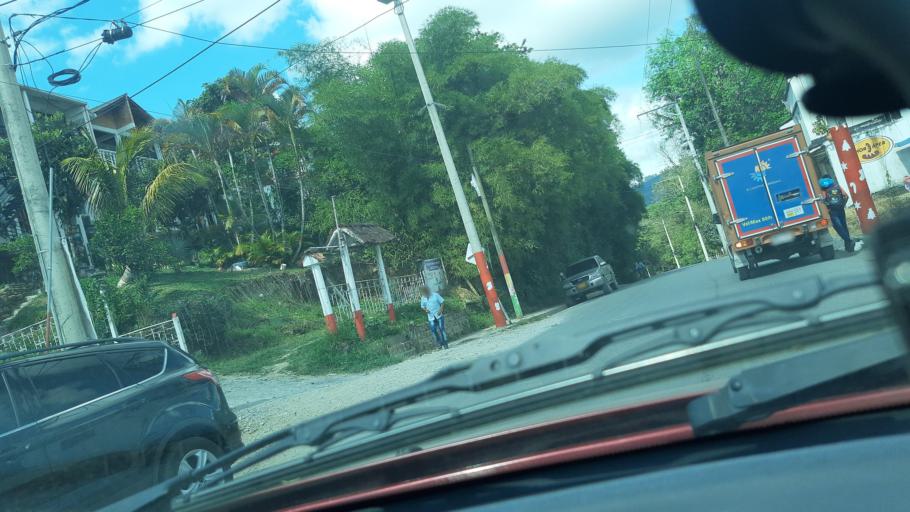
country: CO
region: Boyaca
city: Moniquira
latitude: 5.8697
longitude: -73.5741
